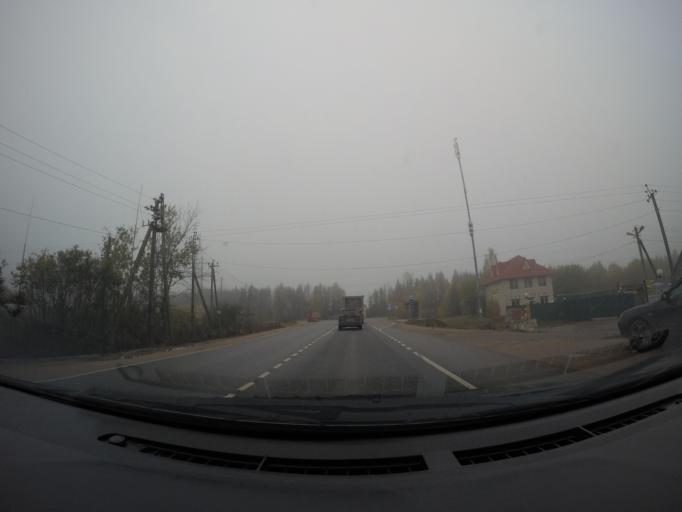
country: RU
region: Moskovskaya
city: Rumyantsevo
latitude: 55.8783
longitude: 36.5665
